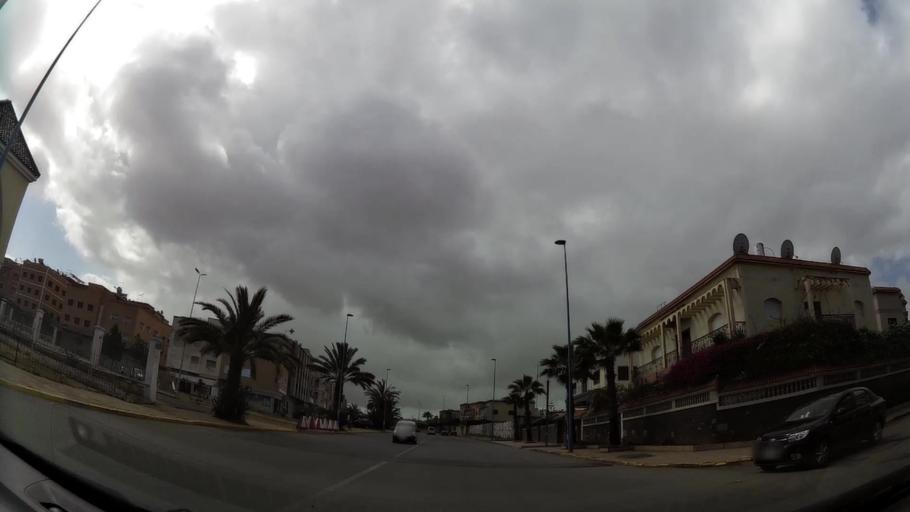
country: MA
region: Grand Casablanca
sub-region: Casablanca
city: Casablanca
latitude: 33.5453
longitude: -7.6023
